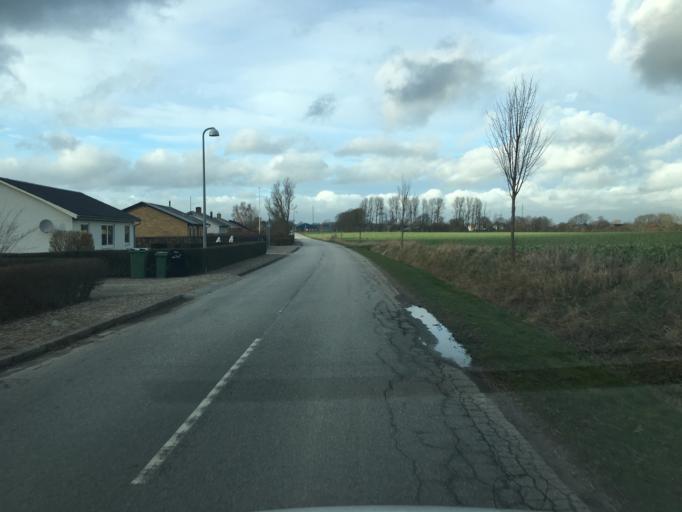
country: DK
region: South Denmark
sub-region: Sonderborg Kommune
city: Grasten
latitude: 54.9729
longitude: 9.5173
